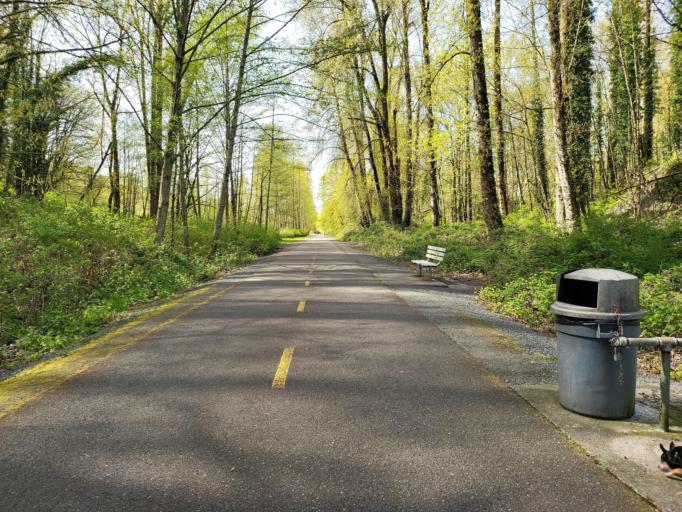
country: US
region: Washington
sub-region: King County
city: Renton
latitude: 47.4768
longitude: -122.1905
